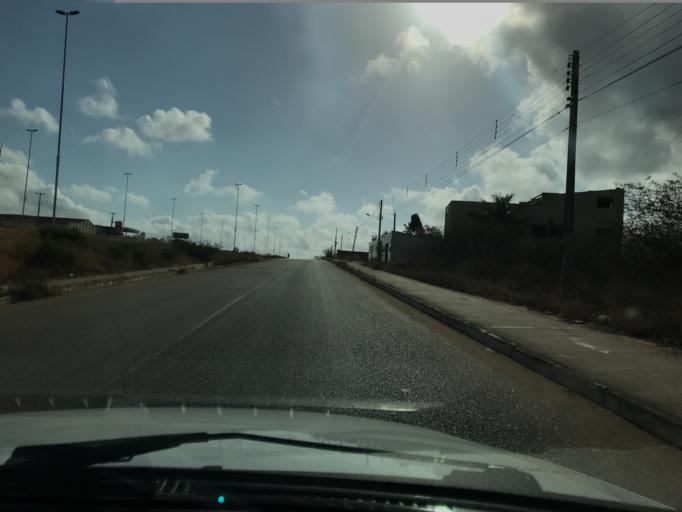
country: BR
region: Pernambuco
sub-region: Bezerros
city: Bezerros
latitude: -8.2374
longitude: -35.7360
